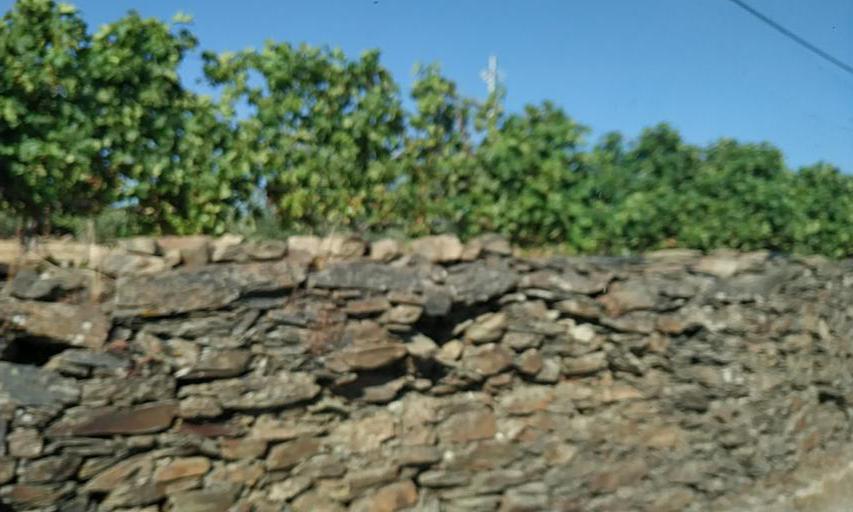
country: PT
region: Viseu
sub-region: Sao Joao da Pesqueira
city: Sao Joao da Pesqueira
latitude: 41.1866
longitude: -7.4407
